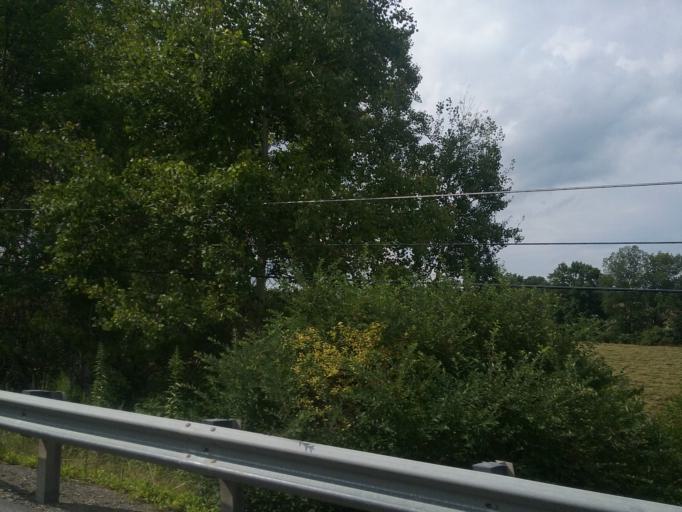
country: US
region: Pennsylvania
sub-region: Tioga County
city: Wellsboro
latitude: 41.7649
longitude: -77.2041
